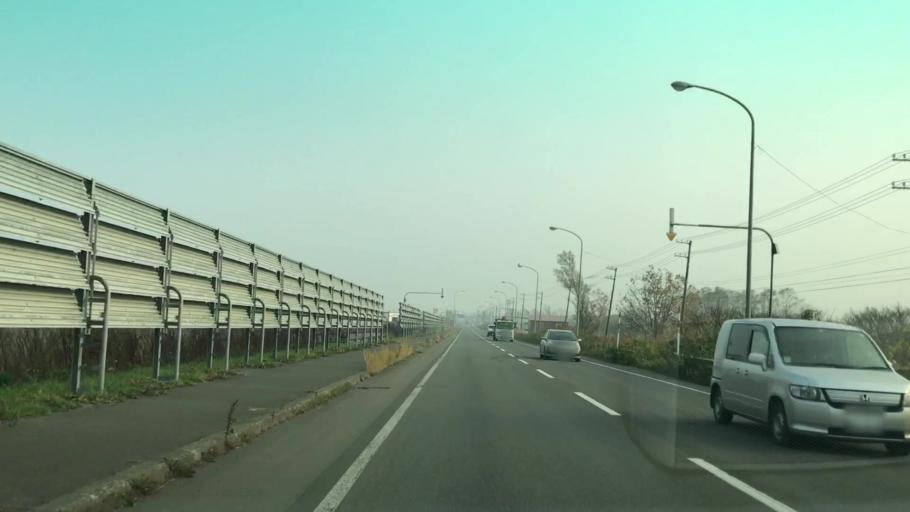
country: JP
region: Hokkaido
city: Ishikari
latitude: 43.2390
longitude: 141.3647
